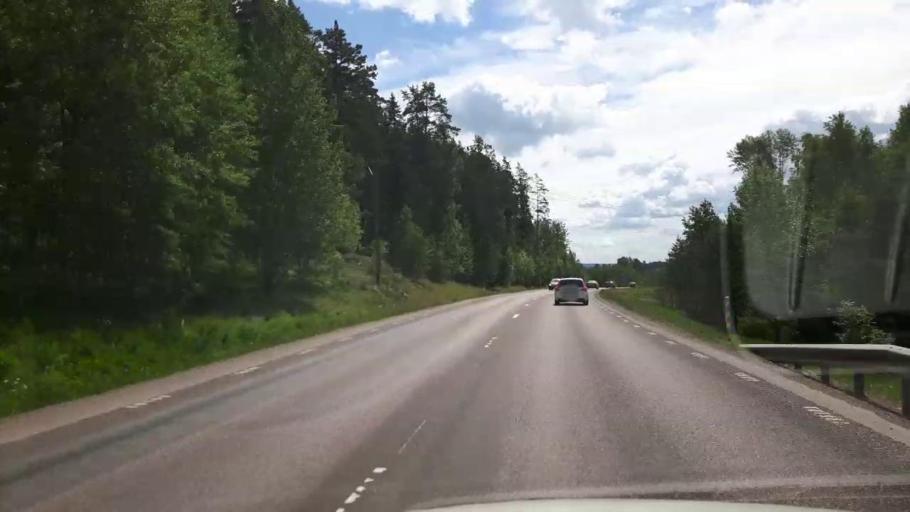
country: SE
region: Dalarna
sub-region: Saters Kommun
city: Saeter
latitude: 60.4560
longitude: 15.8053
